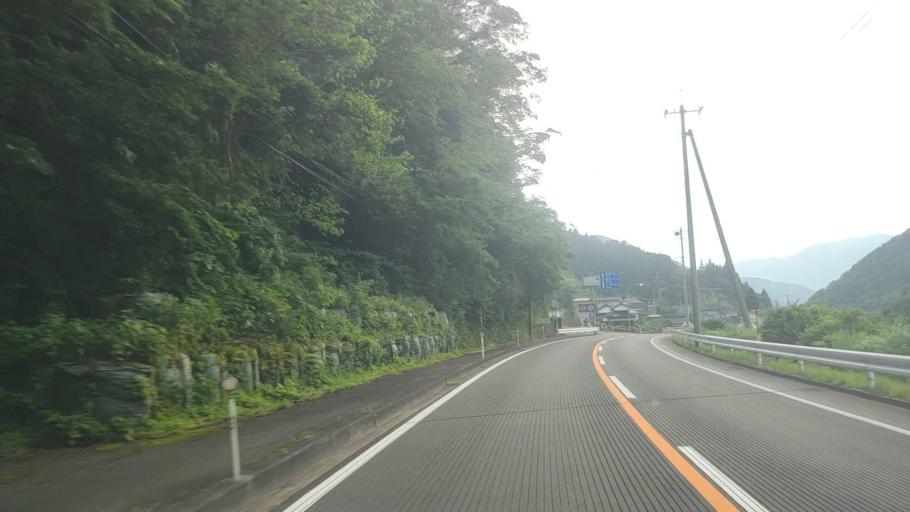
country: JP
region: Tottori
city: Kurayoshi
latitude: 35.3163
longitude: 133.8674
